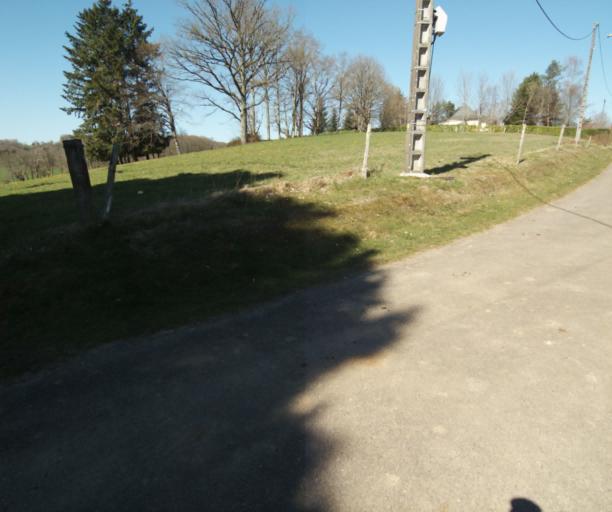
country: FR
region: Limousin
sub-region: Departement de la Correze
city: Saint-Clement
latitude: 45.3009
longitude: 1.7112
